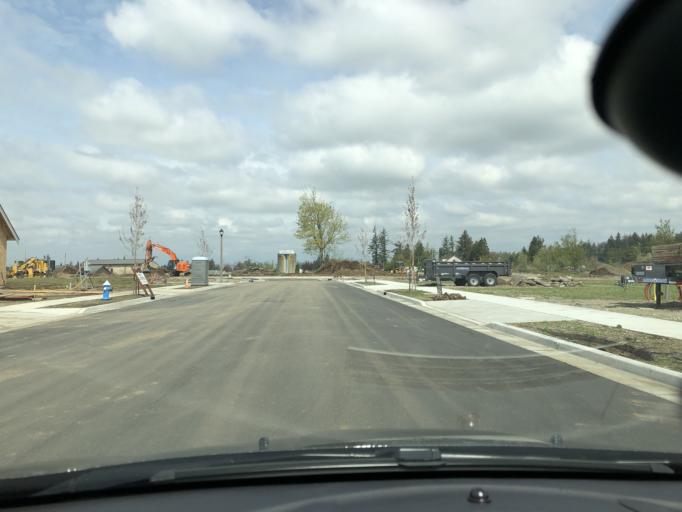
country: US
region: Washington
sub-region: Whatcom County
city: Lynden
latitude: 48.9602
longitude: -122.4043
